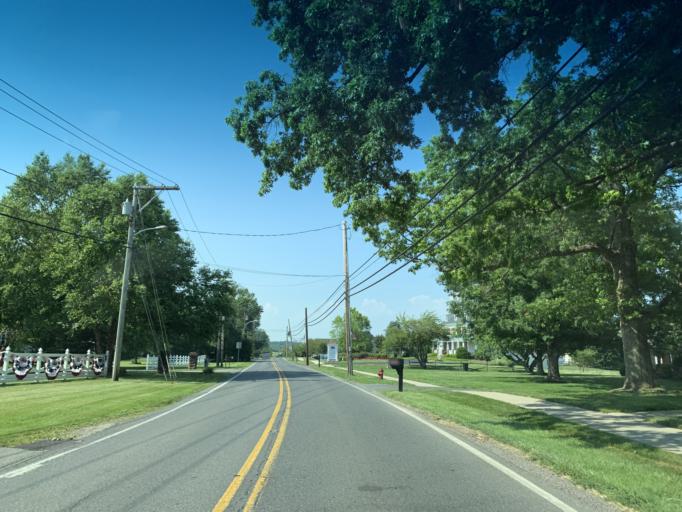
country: US
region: Maryland
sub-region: Montgomery County
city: Poolesville
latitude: 39.1490
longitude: -77.4157
